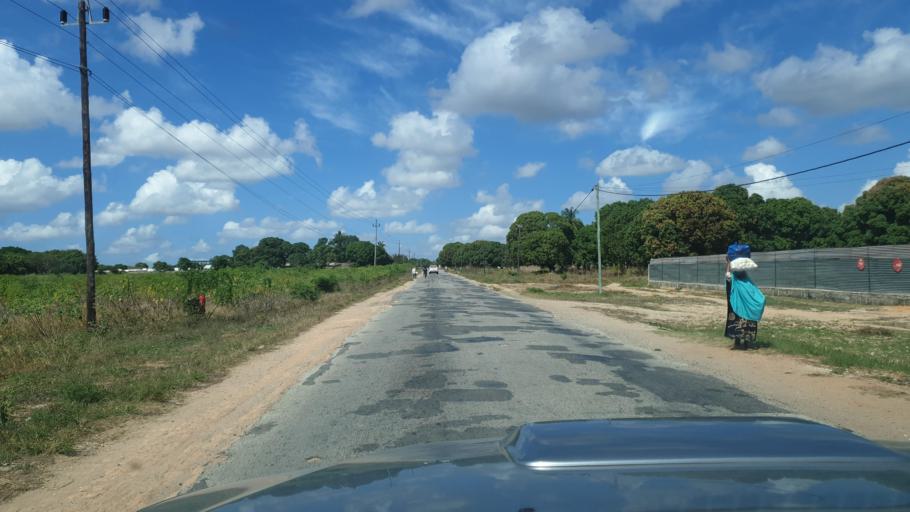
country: MZ
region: Nampula
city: Nacala
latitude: -14.5001
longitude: 40.6966
